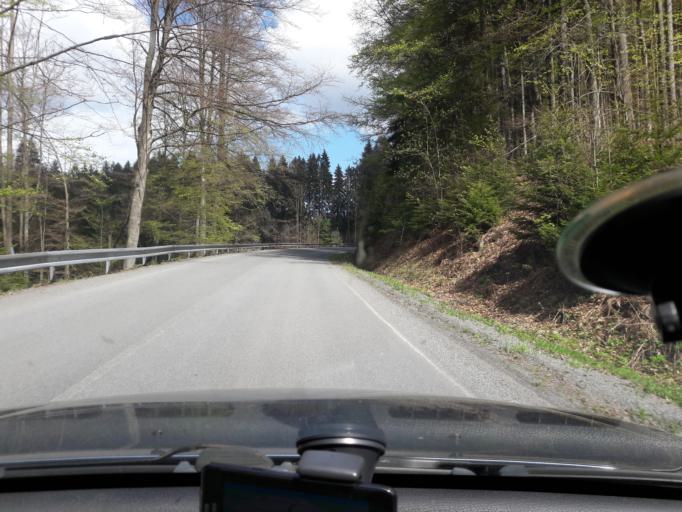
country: SK
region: Banskobystricky
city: Hrinova
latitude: 48.6403
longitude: 19.5935
